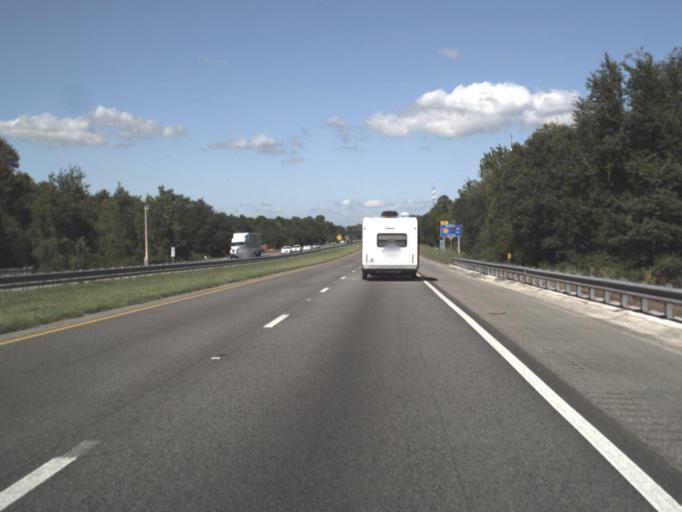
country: US
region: Florida
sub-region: Osceola County
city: Saint Cloud
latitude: 28.0820
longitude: -81.2598
